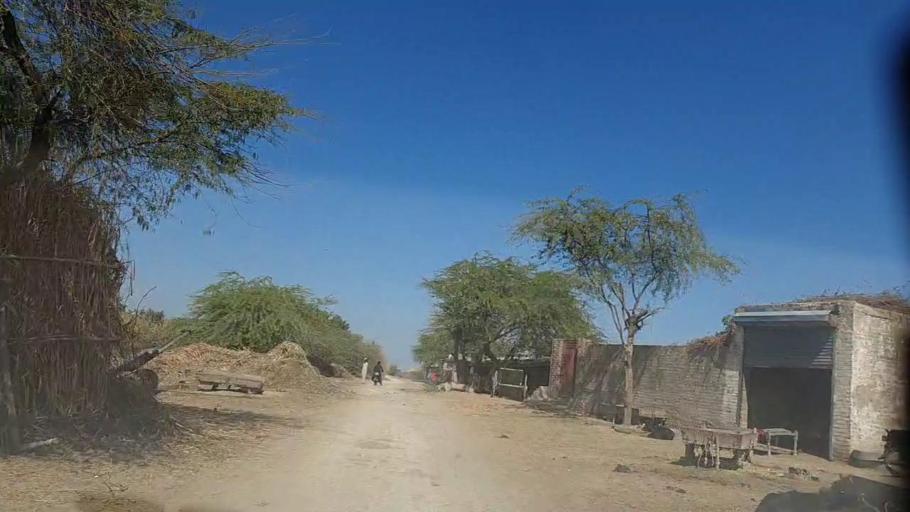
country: PK
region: Sindh
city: Digri
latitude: 25.1821
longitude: 69.0485
